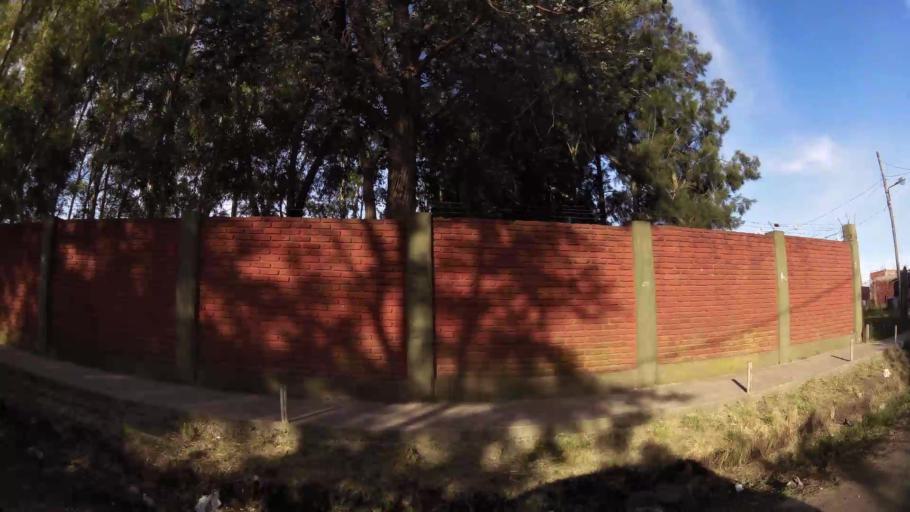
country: AR
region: Buenos Aires
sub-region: Partido de Almirante Brown
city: Adrogue
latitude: -34.8176
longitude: -58.3301
